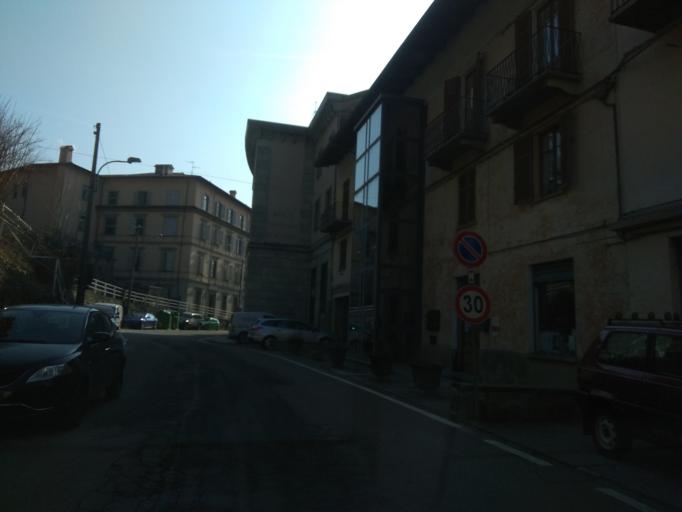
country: IT
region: Piedmont
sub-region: Provincia di Biella
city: Mosso Santa Maria
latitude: 45.6471
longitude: 8.1349
